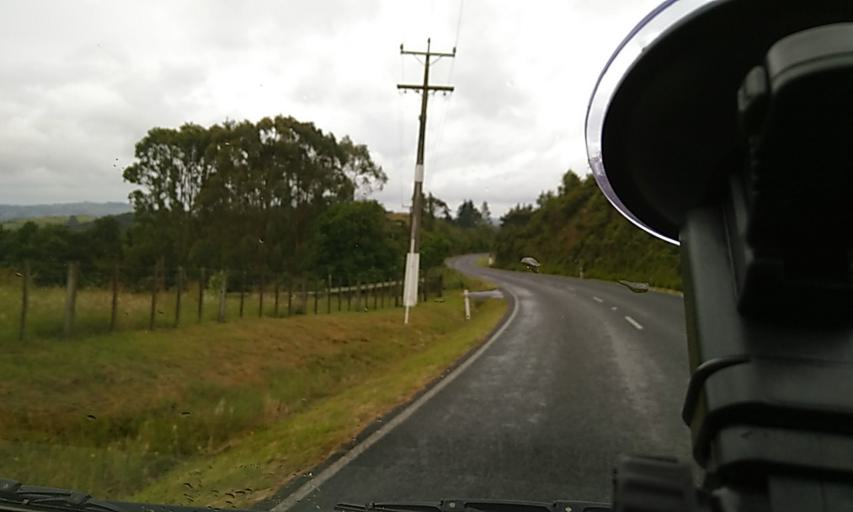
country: NZ
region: Auckland
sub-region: Auckland
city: Pukekohe East
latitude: -37.3186
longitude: 174.9367
